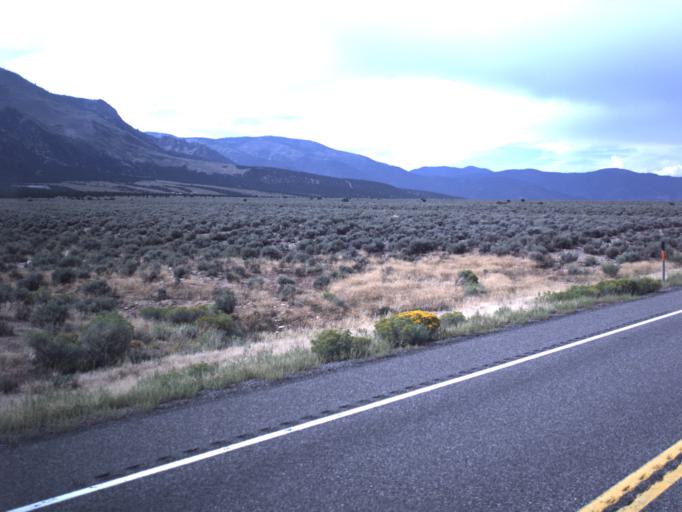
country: US
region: Utah
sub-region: Piute County
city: Junction
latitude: 38.3690
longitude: -112.2250
